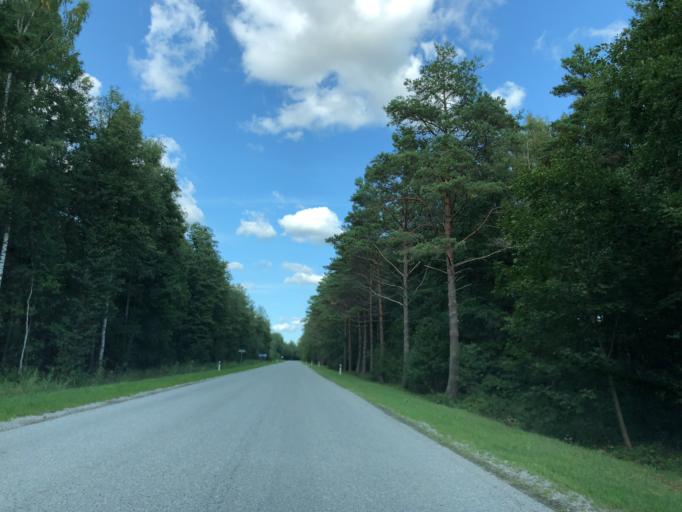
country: EE
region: Hiiumaa
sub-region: Kaerdla linn
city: Kardla
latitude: 58.8151
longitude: 22.7359
